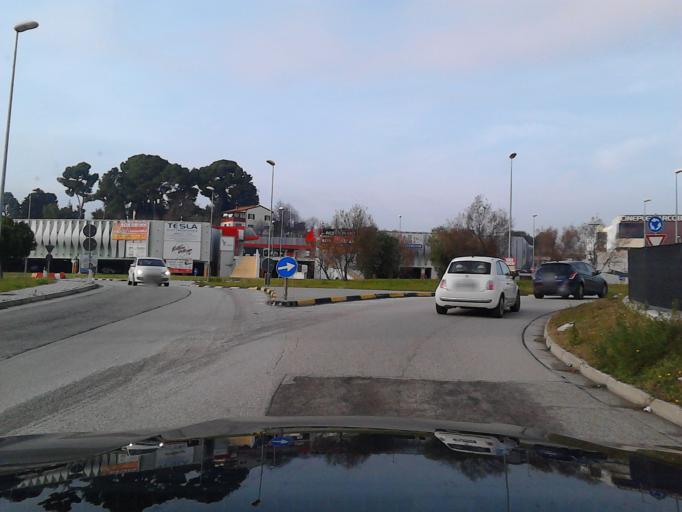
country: IT
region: Abruzzo
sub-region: Provincia di Teramo
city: Villa Rosa
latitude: 42.8354
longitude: 13.8992
